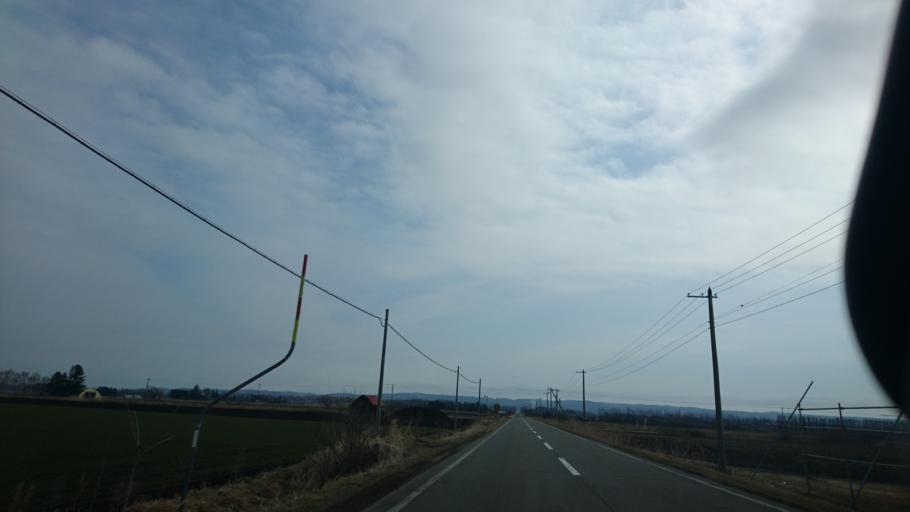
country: JP
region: Hokkaido
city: Otofuke
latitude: 43.0394
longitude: 143.2286
